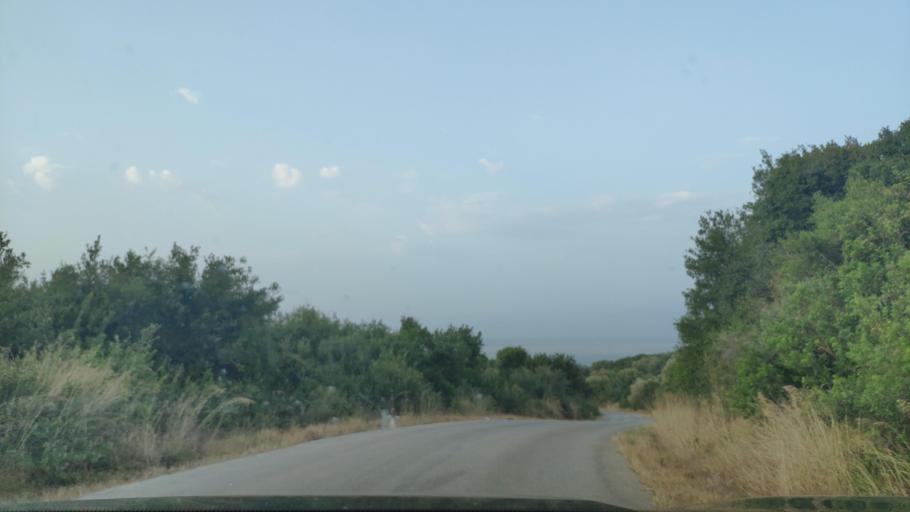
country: GR
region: West Greece
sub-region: Nomos Aitolias kai Akarnanias
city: Monastirakion
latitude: 38.9194
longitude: 20.9786
